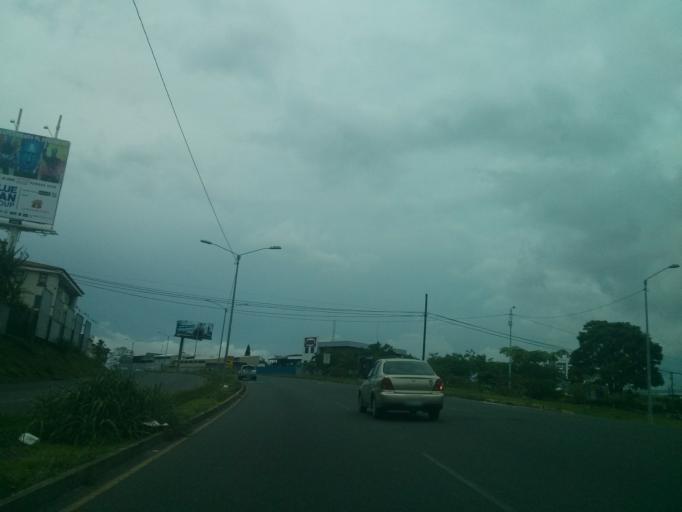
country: CR
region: San Jose
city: Colima
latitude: 9.9464
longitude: -84.1063
